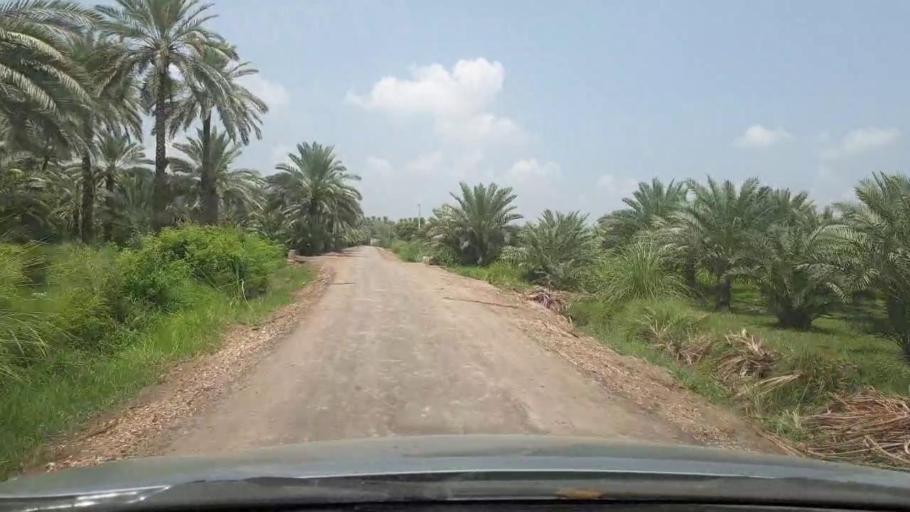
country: PK
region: Sindh
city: Khairpur
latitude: 27.4695
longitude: 68.7350
